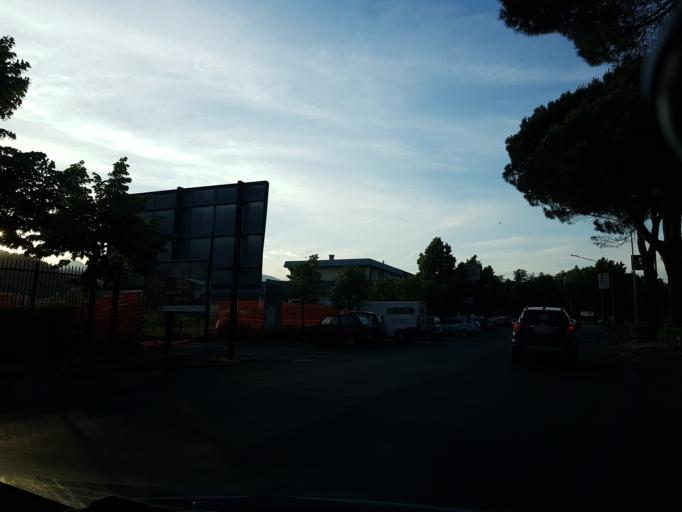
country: IT
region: Tuscany
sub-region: Provincia di Massa-Carrara
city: Aulla
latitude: 44.2176
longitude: 9.9663
